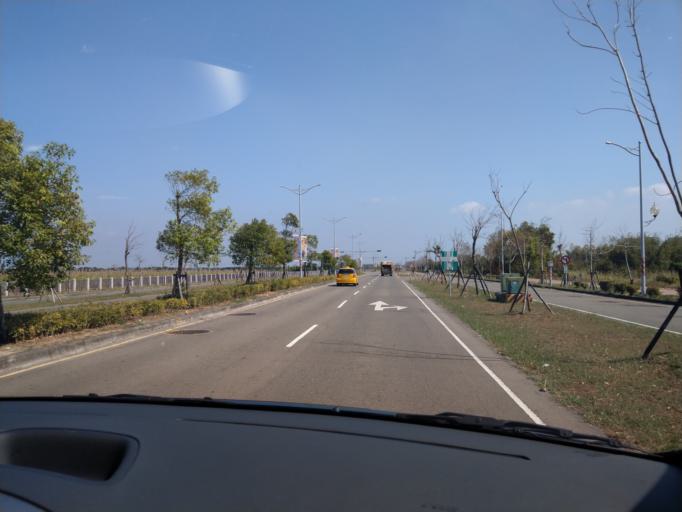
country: TW
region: Taiwan
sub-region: Chiayi
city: Taibao
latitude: 23.4679
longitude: 120.3066
